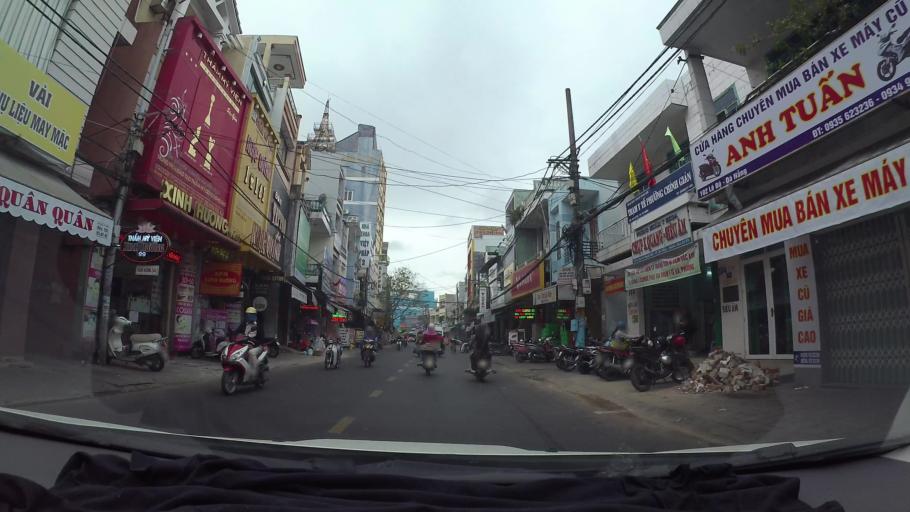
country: VN
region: Da Nang
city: Thanh Khe
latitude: 16.0680
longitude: 108.2015
